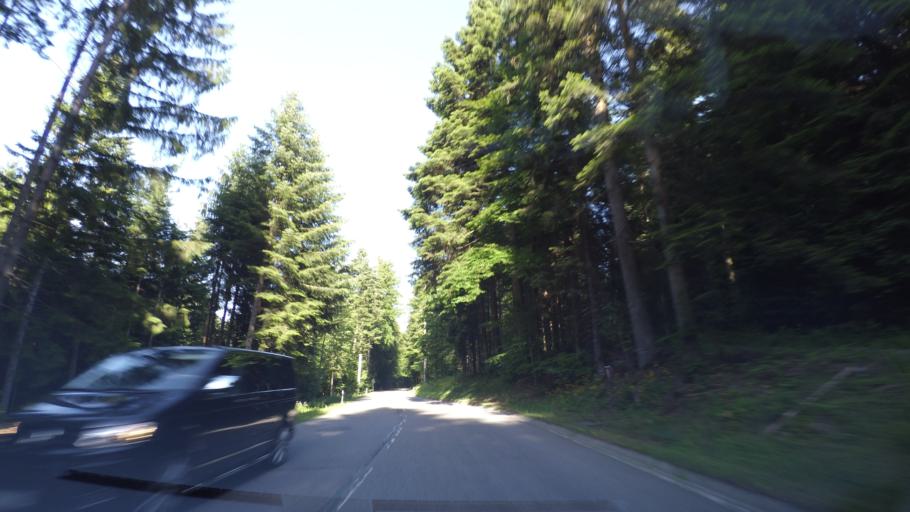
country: DE
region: Baden-Wuerttemberg
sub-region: Regierungsbezirk Stuttgart
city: Welzheim
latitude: 48.9000
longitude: 9.6632
